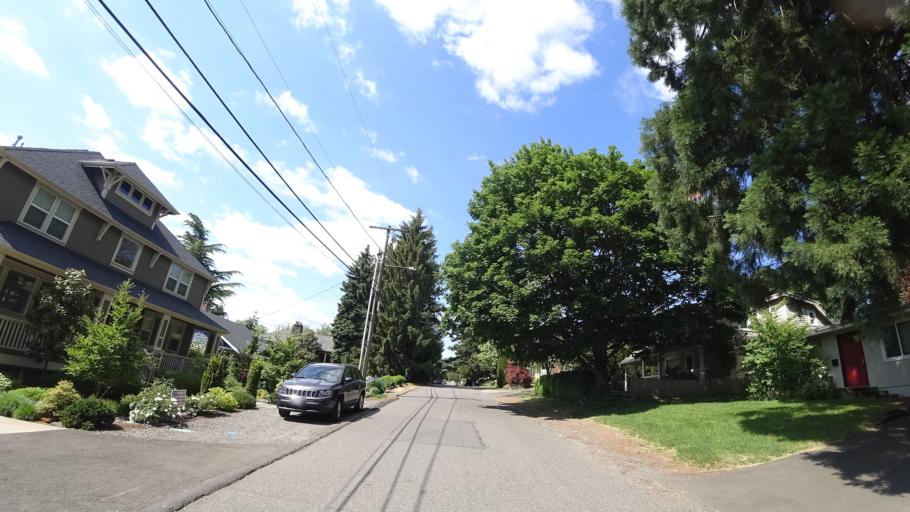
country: US
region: Oregon
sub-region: Washington County
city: Garden Home-Whitford
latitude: 45.4700
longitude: -122.7103
